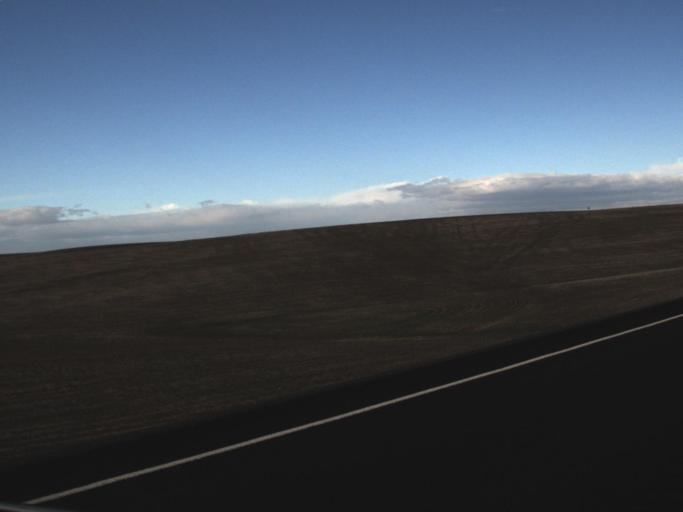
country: US
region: Washington
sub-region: Okanogan County
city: Coulee Dam
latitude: 47.8729
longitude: -118.8413
